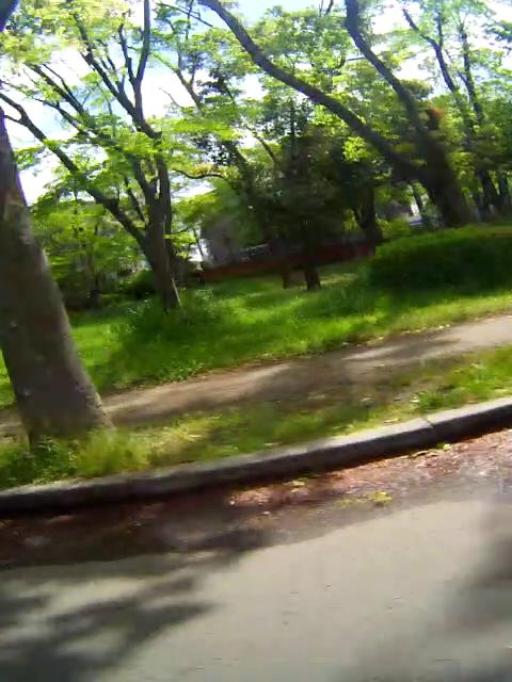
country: JP
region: Osaka
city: Osaka-shi
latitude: 34.7062
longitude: 135.5191
